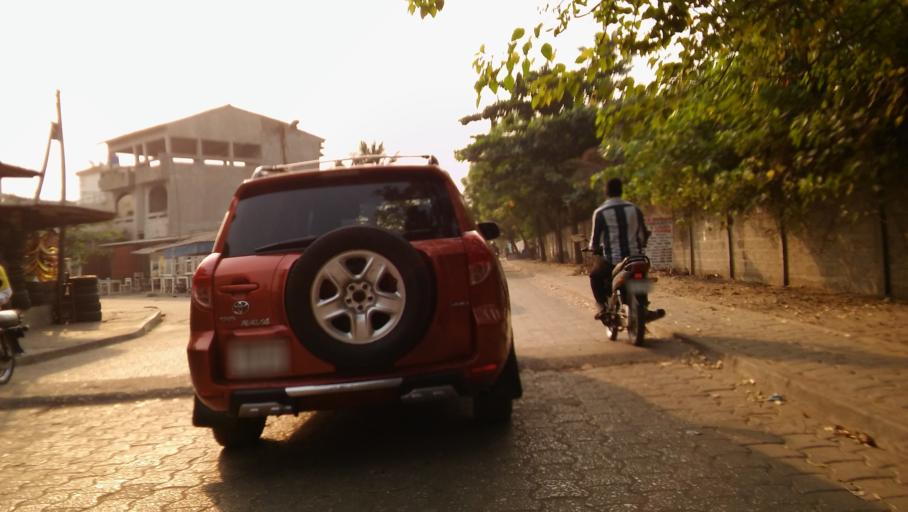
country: BJ
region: Littoral
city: Cotonou
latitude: 6.3793
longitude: 2.3886
